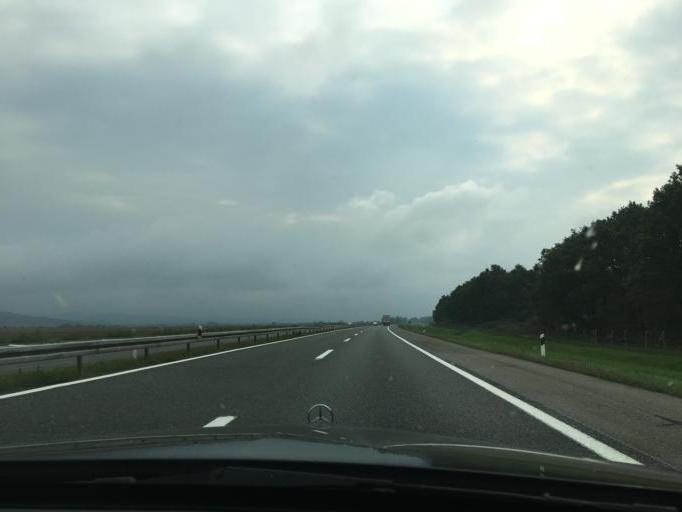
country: HR
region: Sisacko-Moslavacka
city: Novska
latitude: 45.3024
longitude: 17.0469
